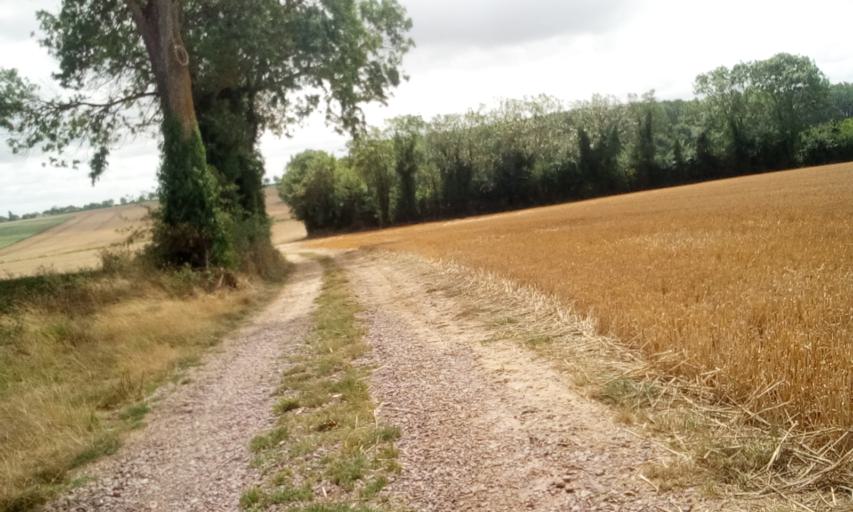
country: FR
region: Lower Normandy
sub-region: Departement du Calvados
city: Cheux
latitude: 49.1867
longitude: -0.5313
